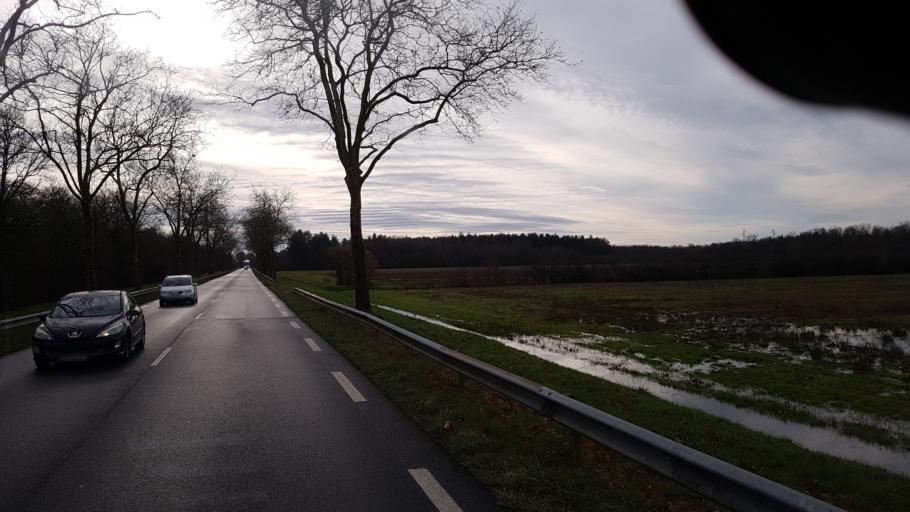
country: FR
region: Centre
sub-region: Departement du Loiret
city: Saint-Cyr-en-Val
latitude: 47.7865
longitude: 1.9342
